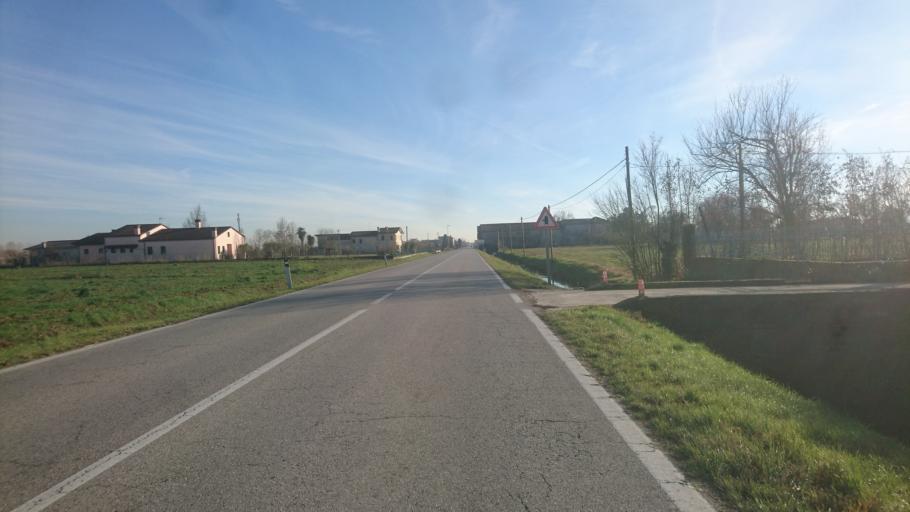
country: IT
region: Veneto
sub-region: Provincia di Padova
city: Villafranca Padovana
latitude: 45.5051
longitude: 11.7912
